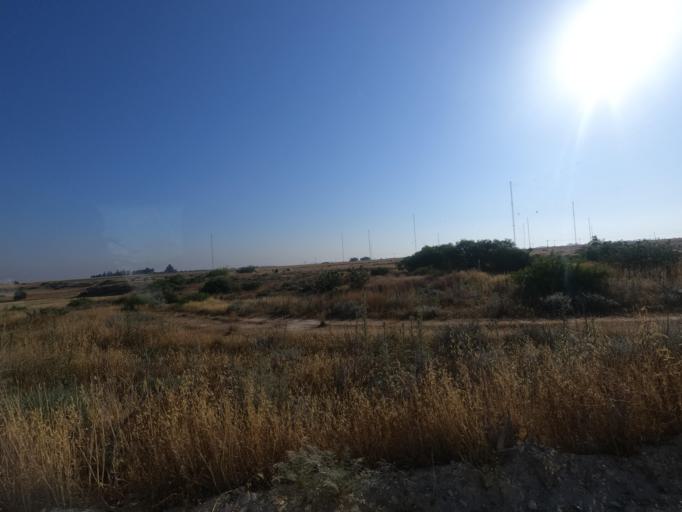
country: CY
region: Ammochostos
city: Acheritou
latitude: 35.0953
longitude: 33.8882
